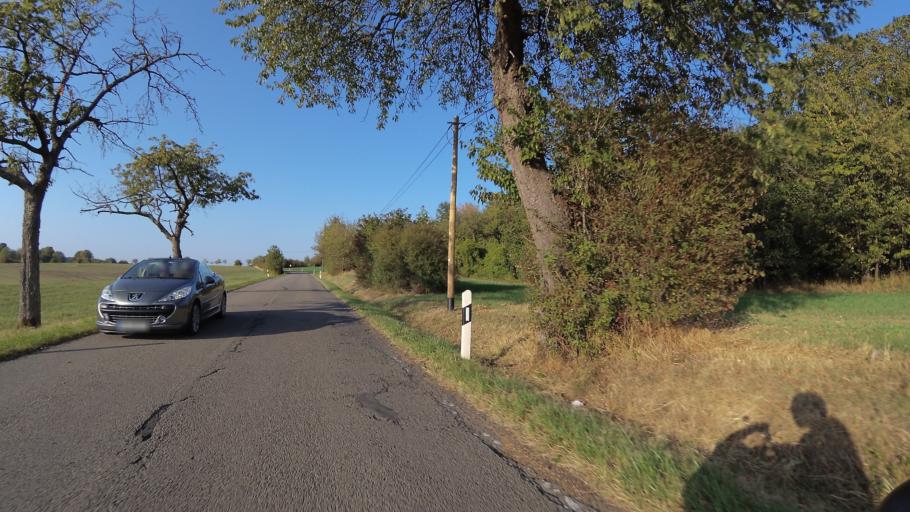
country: DE
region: Saarland
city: Sankt Ingbert
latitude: 49.2317
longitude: 7.1566
